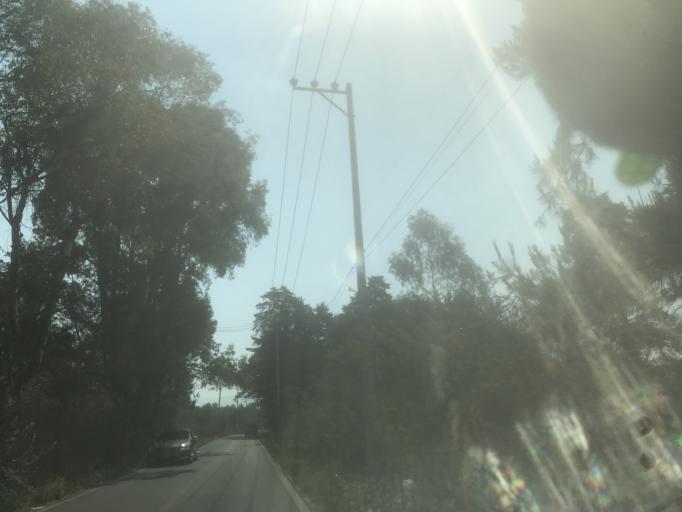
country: MX
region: Mexico
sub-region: Atlautla
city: San Juan Tepecoculco
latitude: 18.9953
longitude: -98.7848
